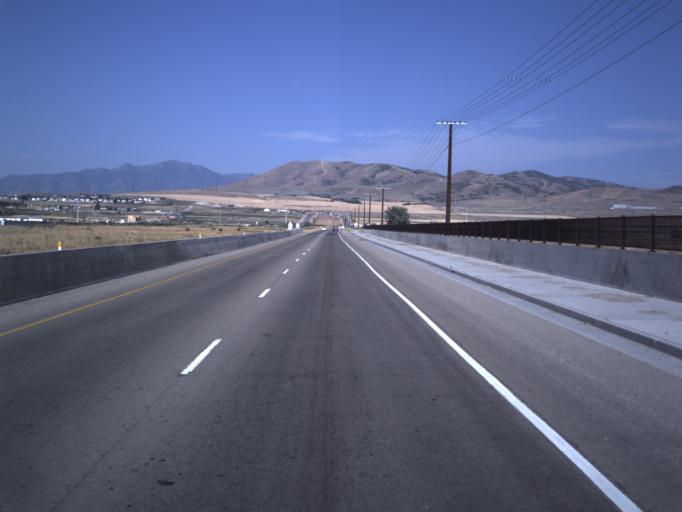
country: US
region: Utah
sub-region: Utah County
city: Lehi
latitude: 40.4132
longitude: -111.8937
